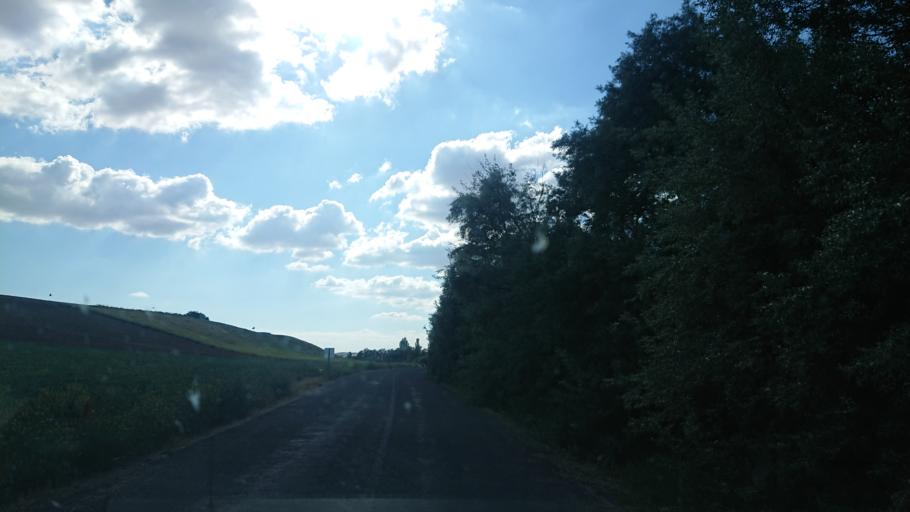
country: TR
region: Aksaray
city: Agacoren
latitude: 38.7577
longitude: 33.9110
